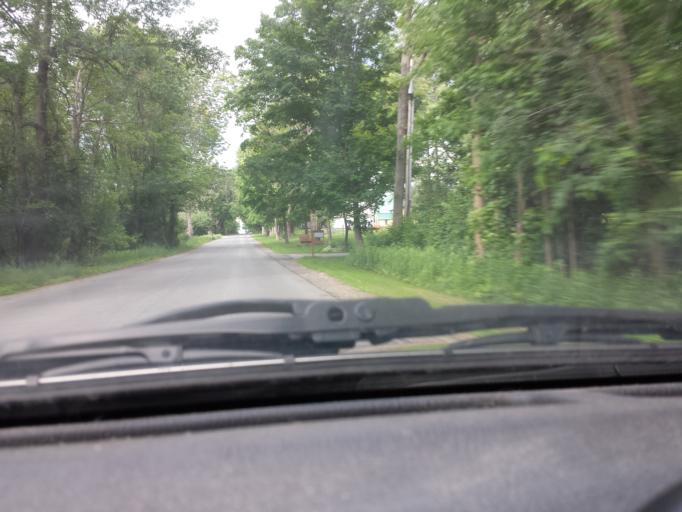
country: US
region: New York
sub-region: St. Lawrence County
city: Norwood
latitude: 44.7190
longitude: -74.9643
